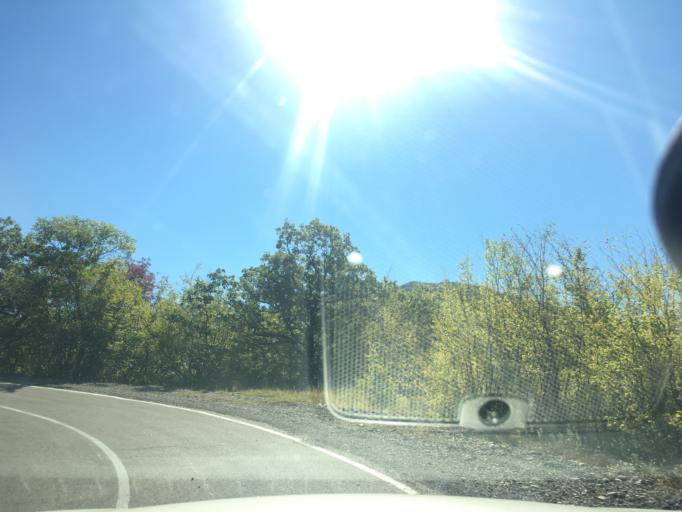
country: GE
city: Didi Lilo
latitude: 41.8638
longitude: 44.9115
